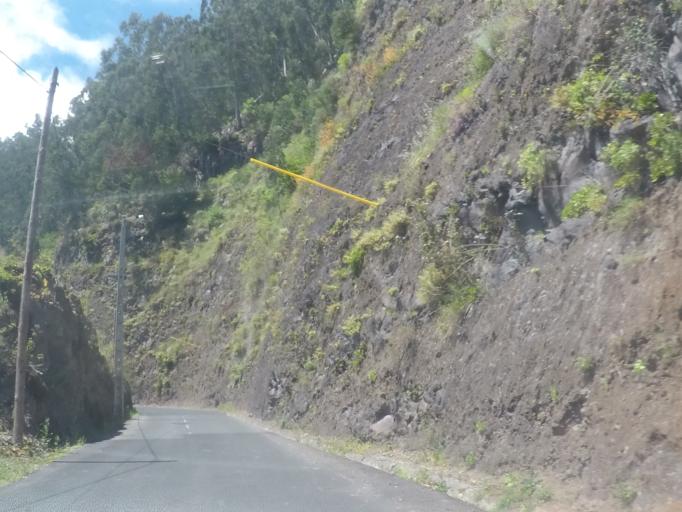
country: PT
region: Madeira
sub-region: Camara de Lobos
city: Curral das Freiras
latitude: 32.6903
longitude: -16.9709
